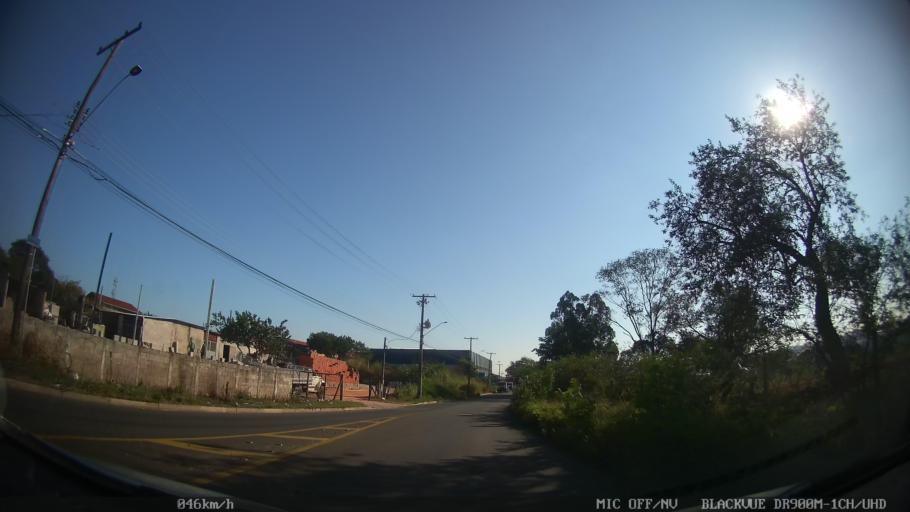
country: BR
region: Sao Paulo
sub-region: Campinas
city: Campinas
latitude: -22.9694
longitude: -47.1106
